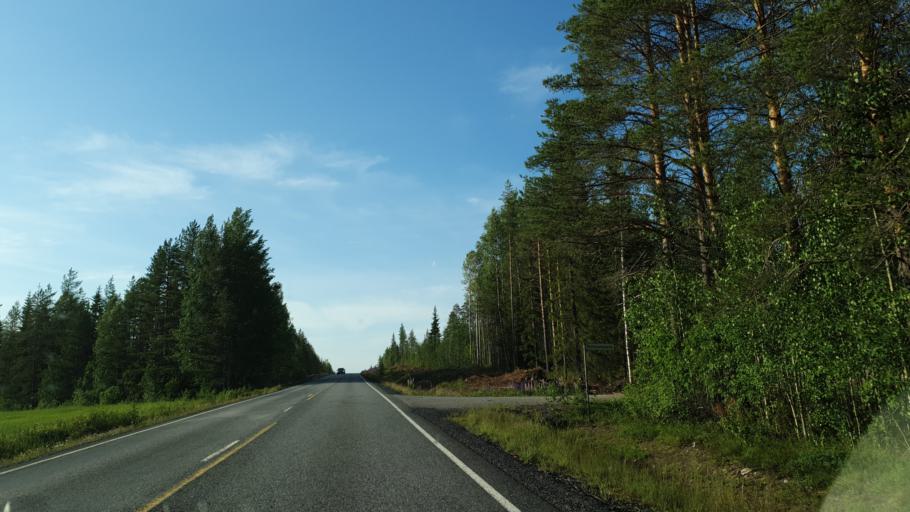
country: FI
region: Kainuu
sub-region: Kehys-Kainuu
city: Kuhmo
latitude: 64.0825
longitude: 29.4849
